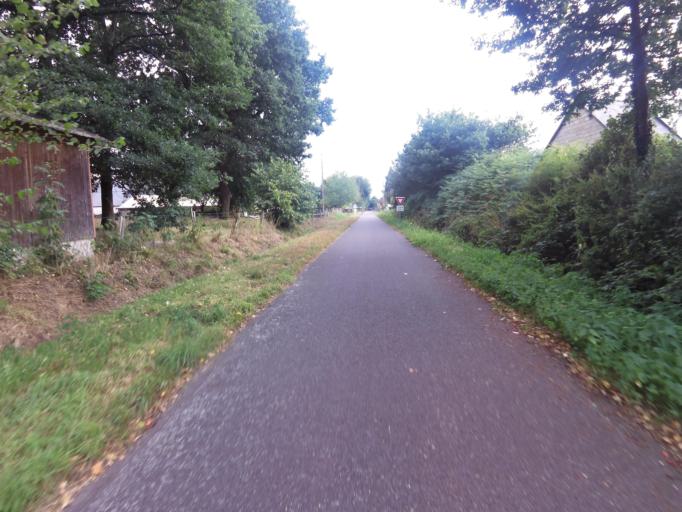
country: FR
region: Brittany
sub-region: Departement du Morbihan
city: Guillac
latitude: 47.8795
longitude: -2.4370
